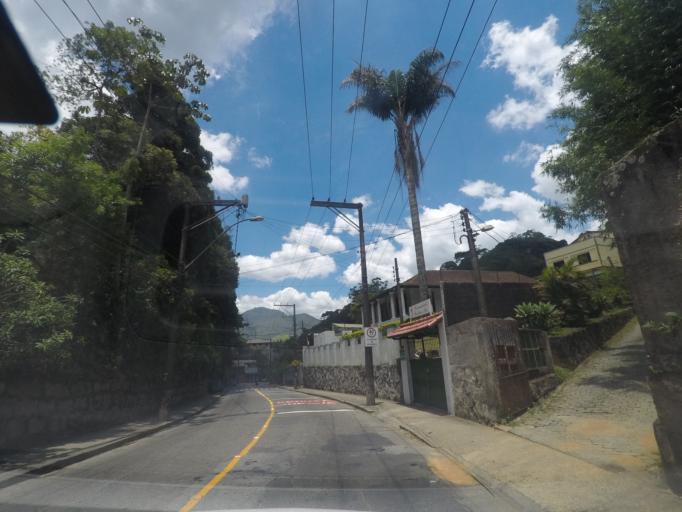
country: BR
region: Rio de Janeiro
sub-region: Petropolis
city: Petropolis
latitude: -22.5009
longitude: -43.1693
